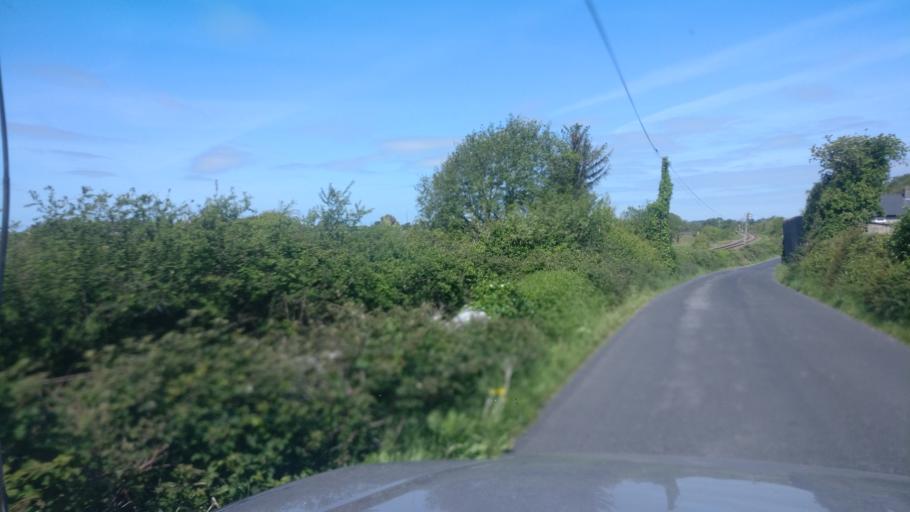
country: IE
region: Connaught
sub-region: County Galway
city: Gort
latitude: 53.0889
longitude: -8.8044
